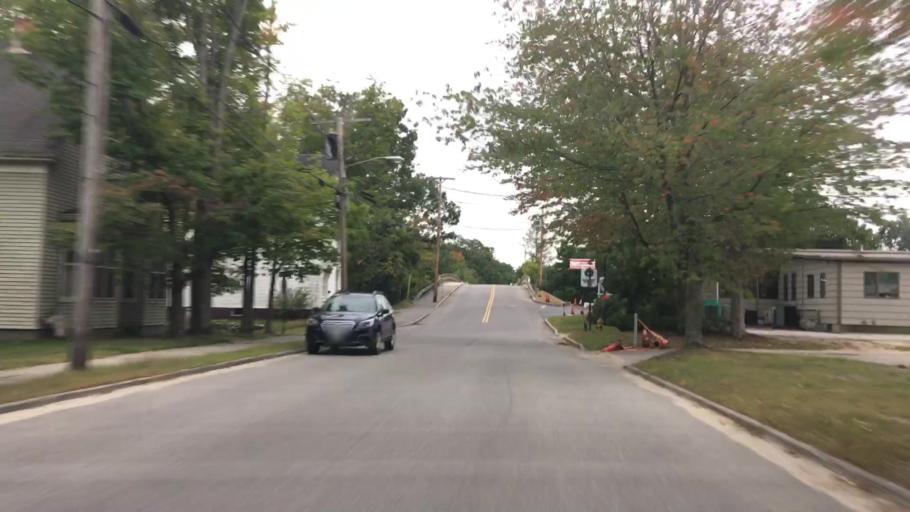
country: US
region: Maine
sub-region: Cumberland County
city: Brunswick
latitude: 43.9121
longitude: -69.9722
